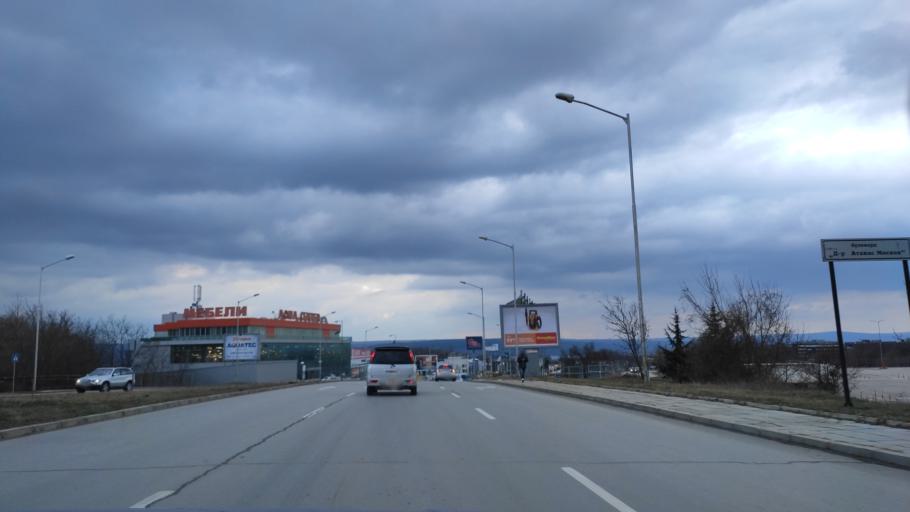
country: BG
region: Varna
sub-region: Obshtina Aksakovo
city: Aksakovo
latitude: 43.2329
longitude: 27.8639
